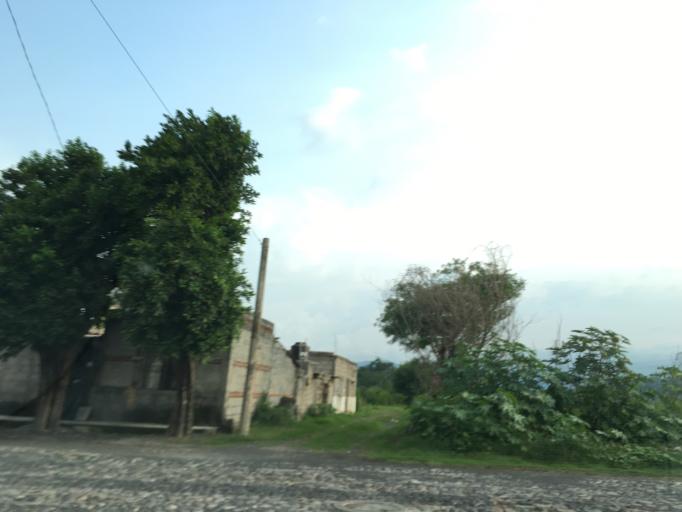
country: MX
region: Nayarit
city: Jala
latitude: 21.0982
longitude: -104.4347
